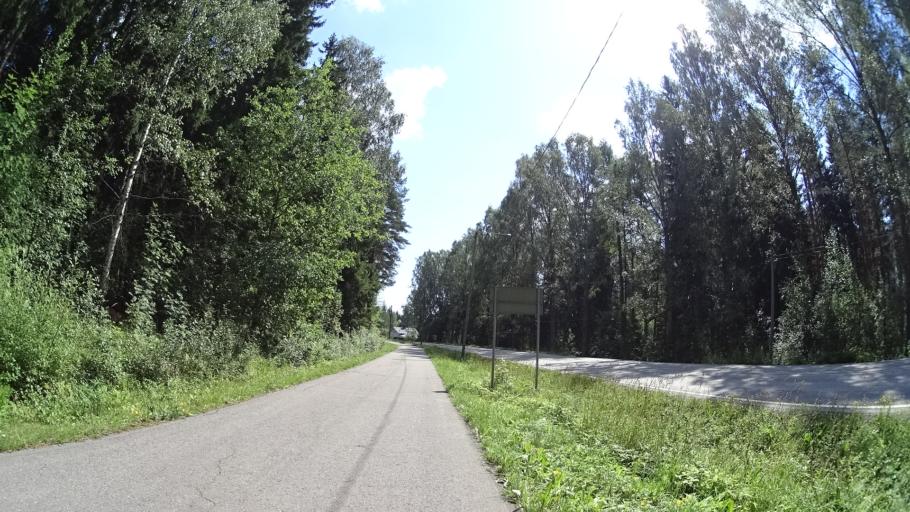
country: FI
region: Uusimaa
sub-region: Helsinki
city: Tuusula
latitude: 60.3601
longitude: 24.9924
